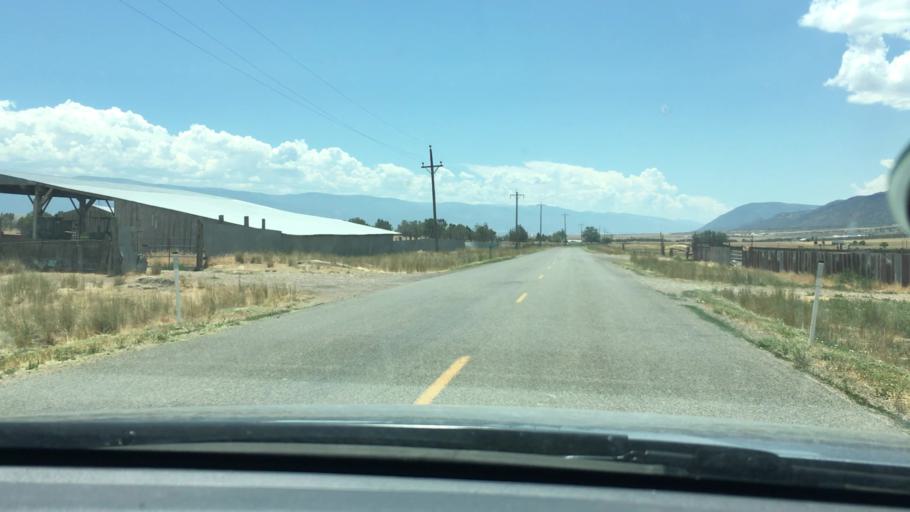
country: US
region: Utah
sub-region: Sanpete County
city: Fountain Green
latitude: 39.6095
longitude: -111.6445
